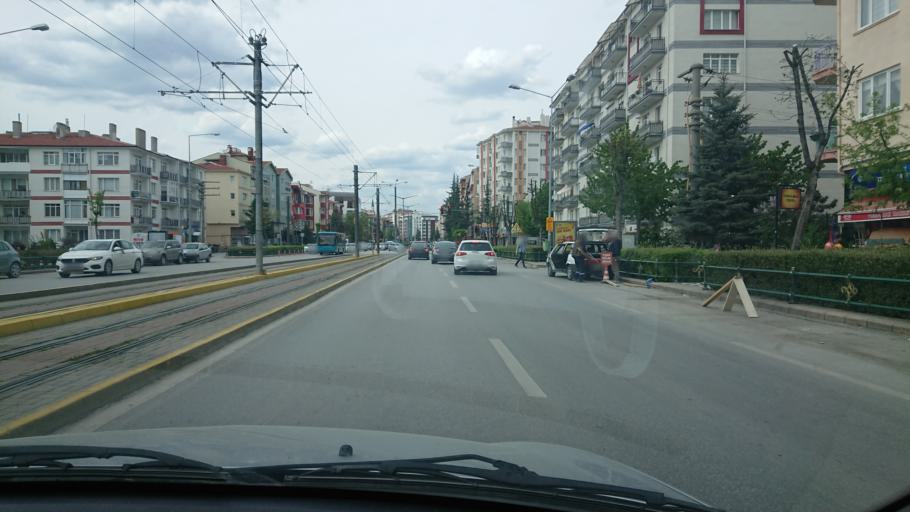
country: TR
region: Eskisehir
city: Eskisehir
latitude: 39.7665
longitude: 30.5007
